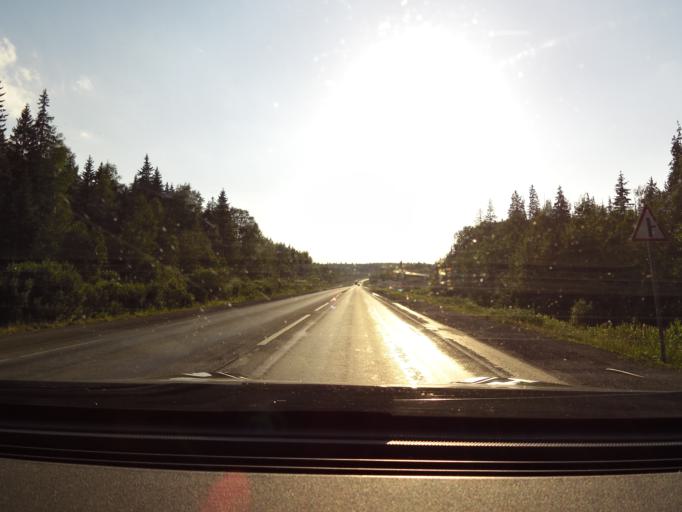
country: RU
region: Sverdlovsk
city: Bilimbay
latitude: 56.8522
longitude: 59.7944
